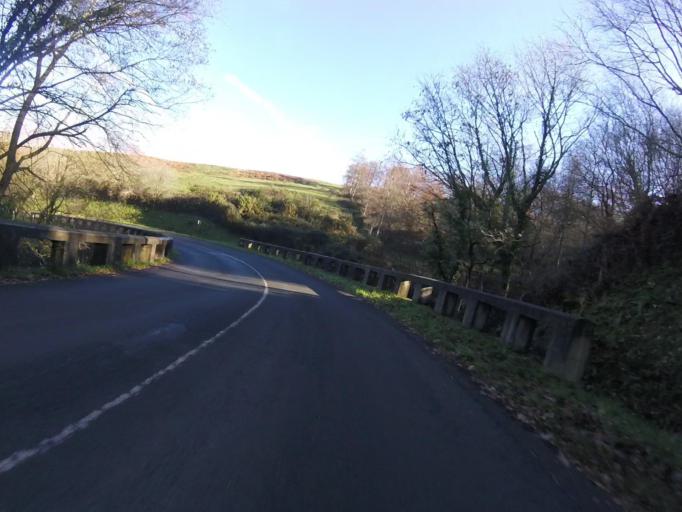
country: ES
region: Basque Country
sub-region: Provincia de Guipuzcoa
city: Fuenterrabia
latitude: 43.3665
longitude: -1.8309
